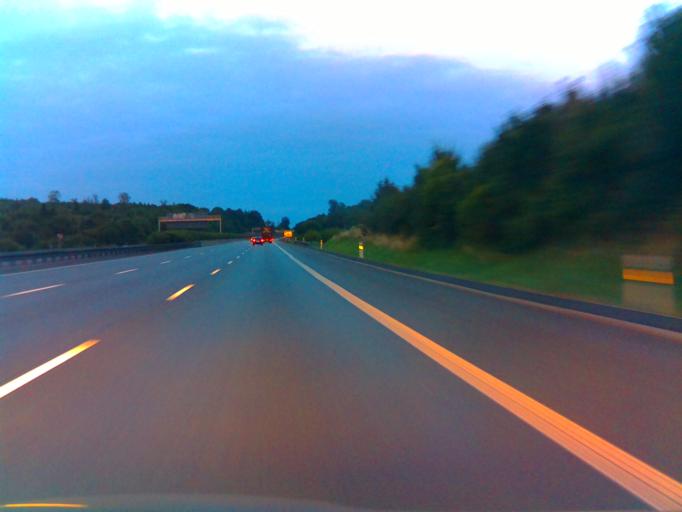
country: DE
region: Thuringia
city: Mellingen
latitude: 50.9273
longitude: 11.3957
